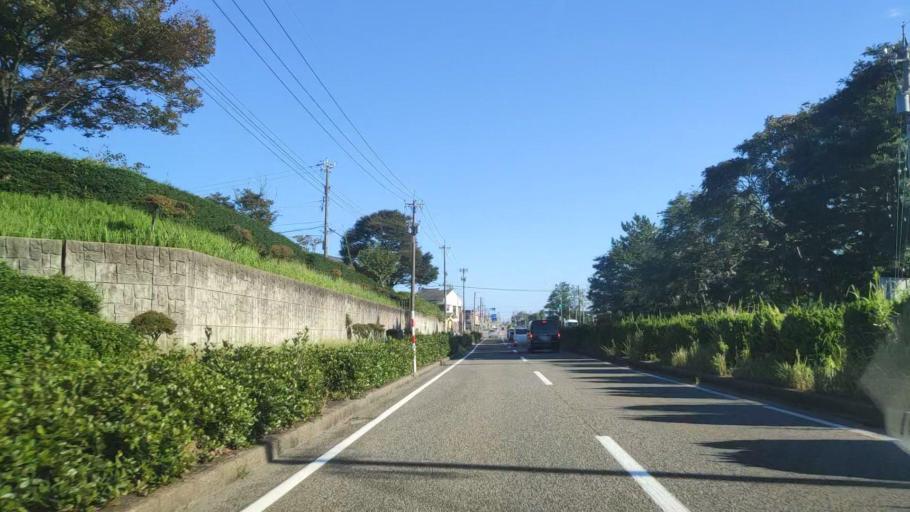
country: JP
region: Ishikawa
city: Tsubata
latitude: 36.7184
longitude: 136.6980
